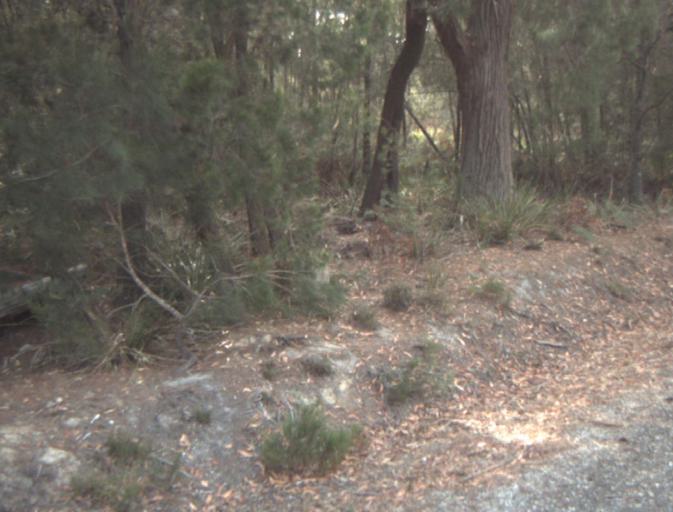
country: AU
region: Tasmania
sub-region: Dorset
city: Bridport
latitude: -41.1220
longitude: 147.2060
